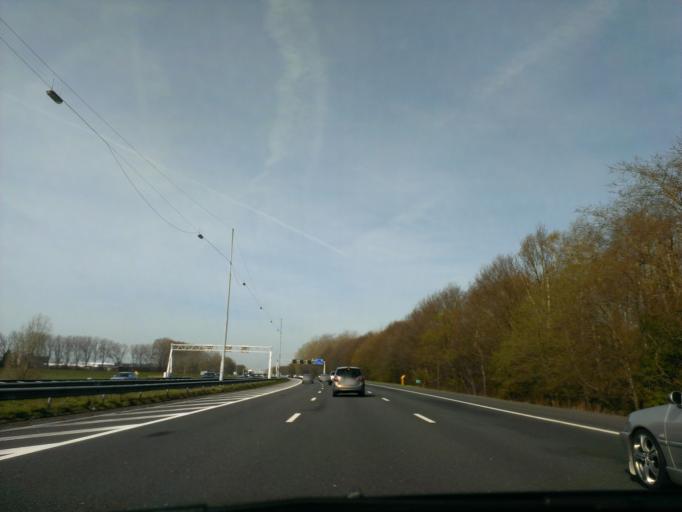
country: NL
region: North Holland
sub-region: Gemeente Naarden
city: Naarden
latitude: 52.3061
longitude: 5.1576
